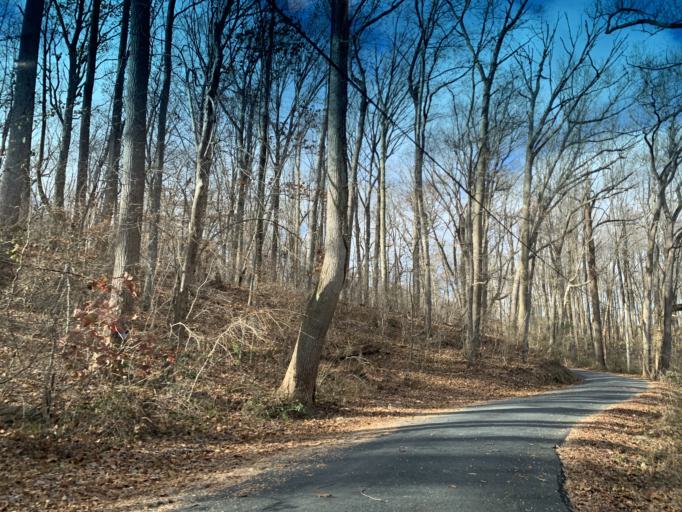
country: US
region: Maryland
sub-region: Harford County
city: Bel Air North
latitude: 39.5915
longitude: -76.4082
